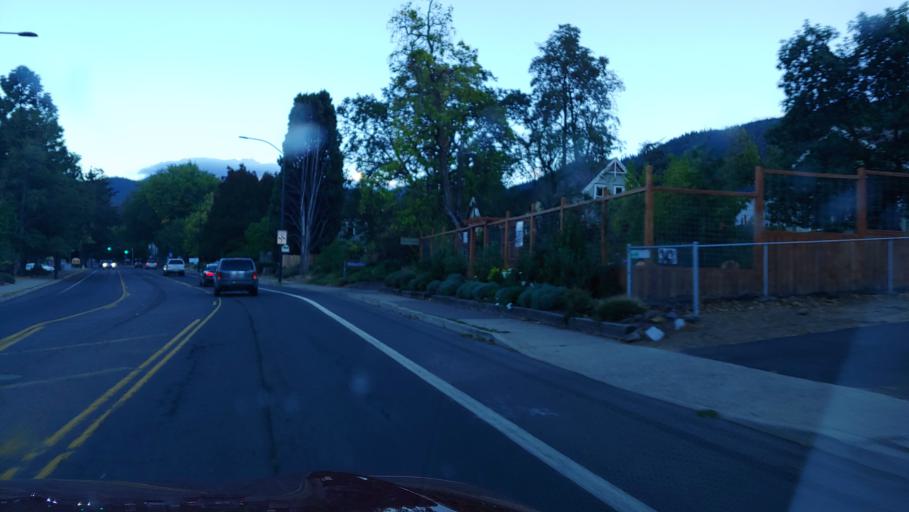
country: US
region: Oregon
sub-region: Jackson County
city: Ashland
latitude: 42.2034
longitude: -122.7196
